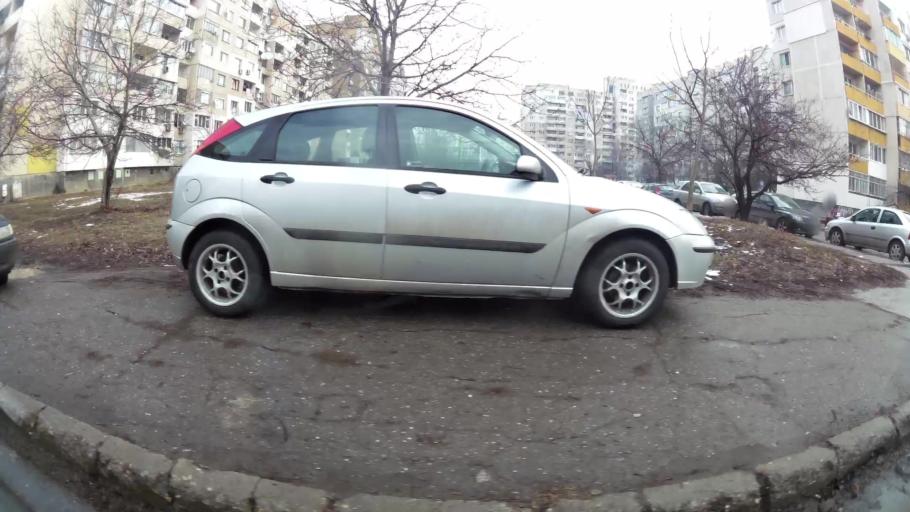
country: BG
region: Sofia-Capital
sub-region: Stolichna Obshtina
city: Sofia
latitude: 42.7105
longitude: 23.2660
